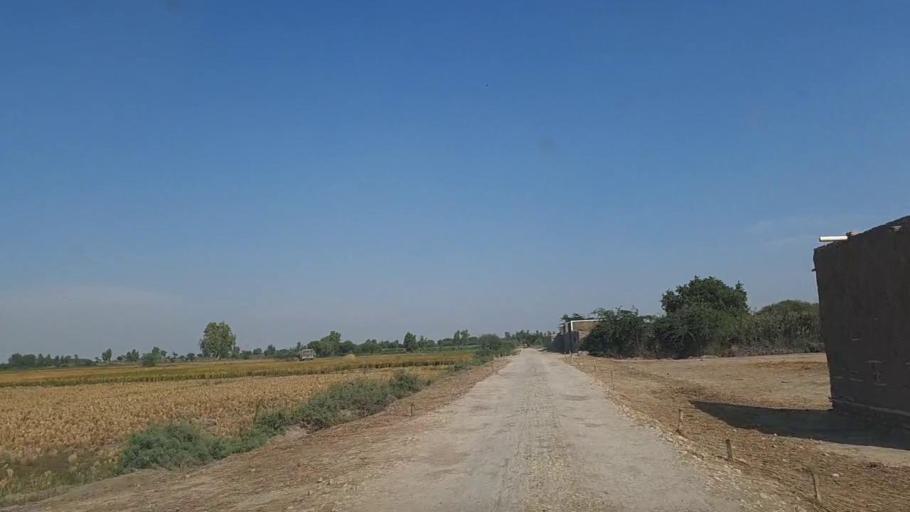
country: PK
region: Sindh
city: Mirpur Batoro
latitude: 24.7975
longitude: 68.2726
